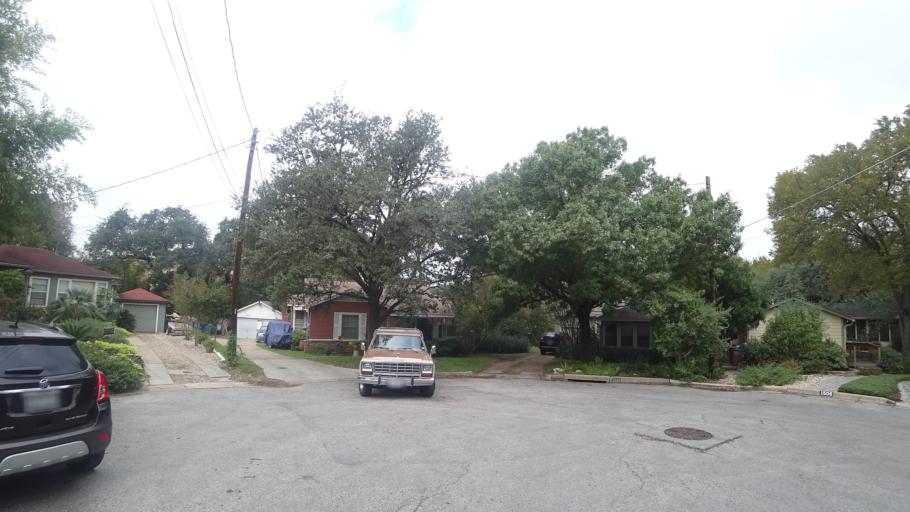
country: US
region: Texas
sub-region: Travis County
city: Austin
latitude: 30.2606
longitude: -97.7610
